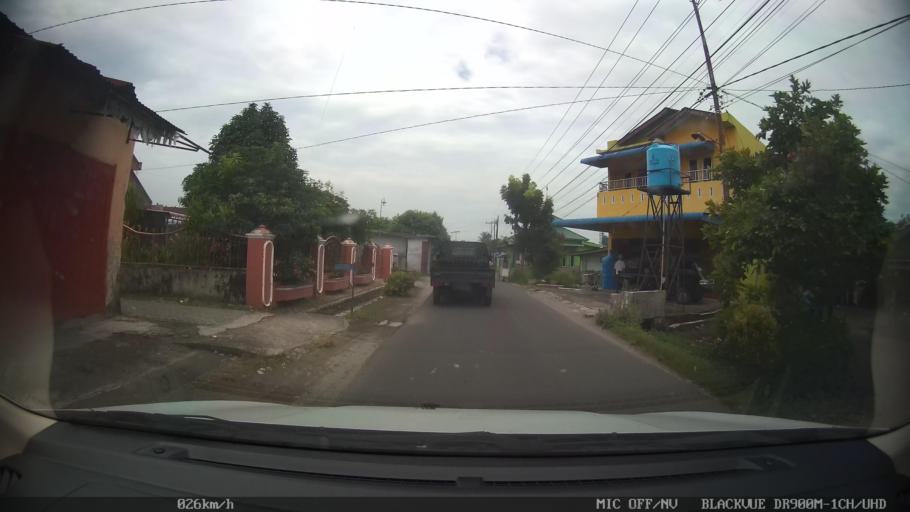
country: ID
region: North Sumatra
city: Binjai
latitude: 3.6264
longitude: 98.5559
